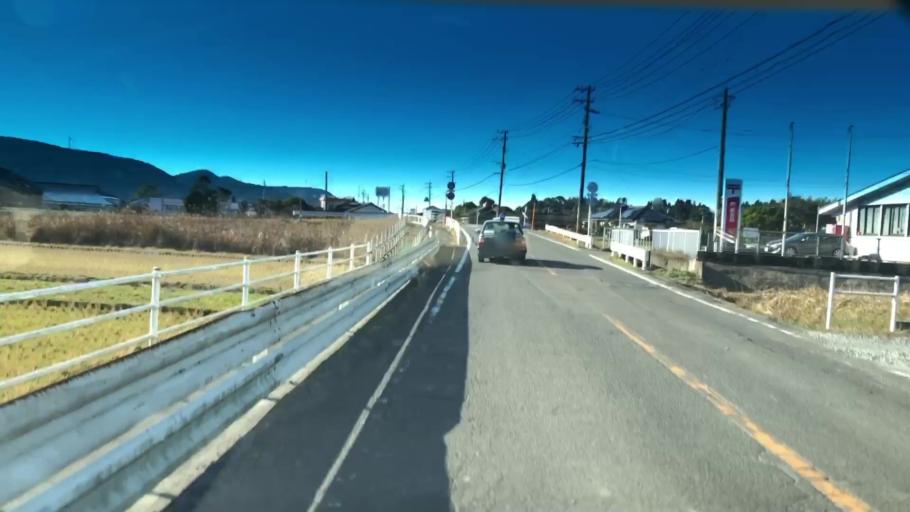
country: JP
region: Kagoshima
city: Satsumasendai
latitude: 31.8233
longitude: 130.2563
